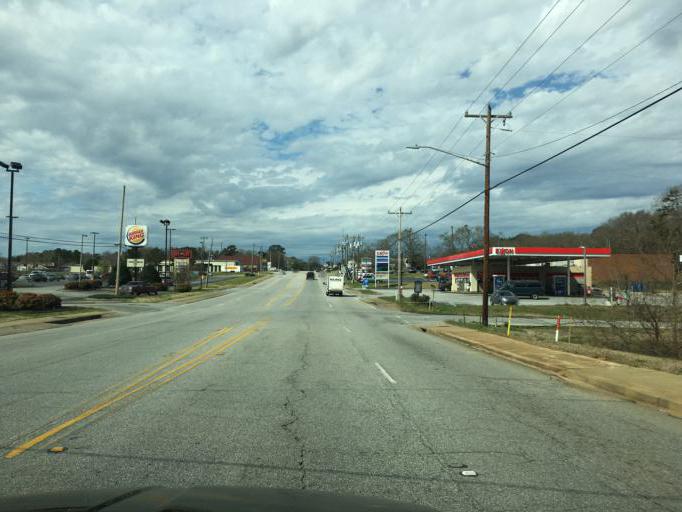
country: US
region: South Carolina
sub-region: Greenville County
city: Fountain Inn
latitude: 34.7013
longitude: -82.2155
